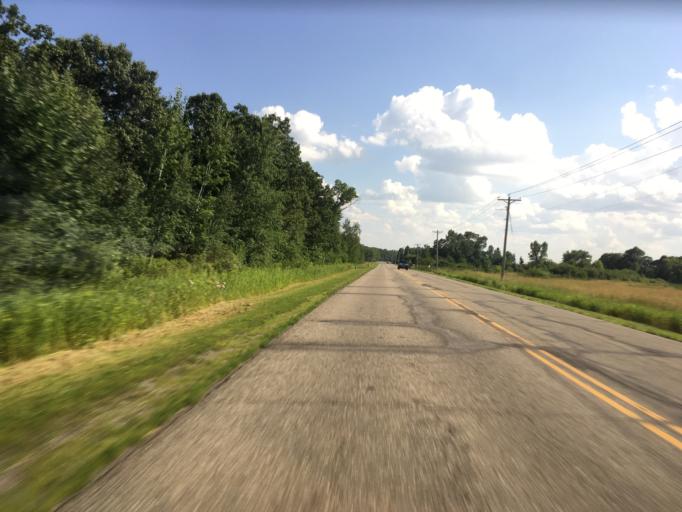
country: US
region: Minnesota
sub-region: Stearns County
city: Sartell
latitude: 45.6457
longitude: -94.2221
